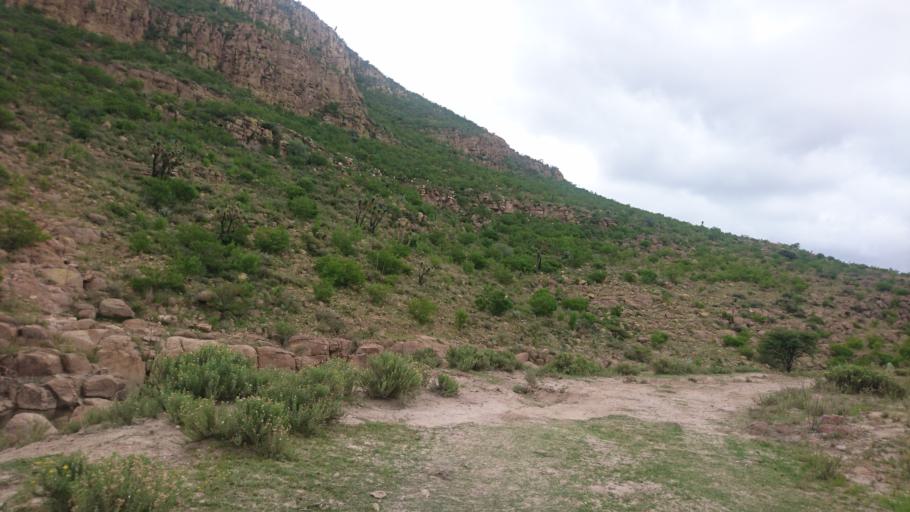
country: MX
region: San Luis Potosi
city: Escalerillas
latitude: 22.0748
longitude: -101.0944
